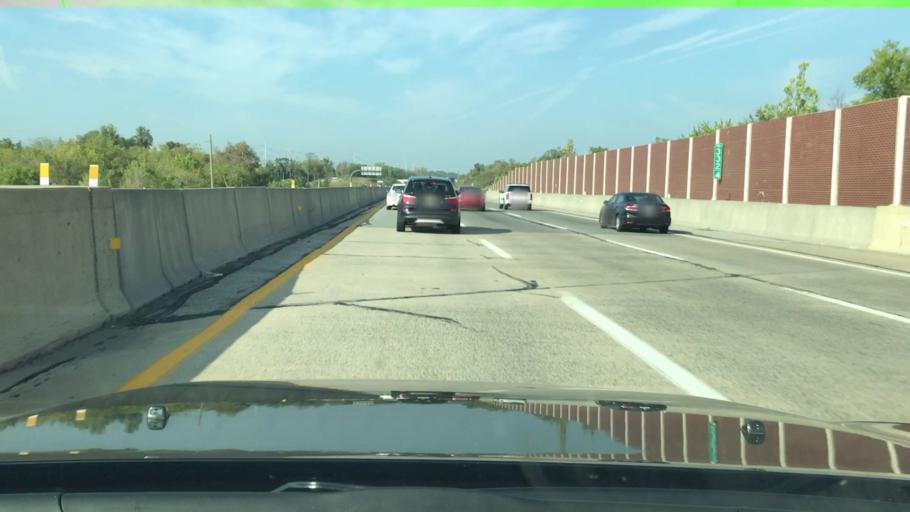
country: US
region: Pennsylvania
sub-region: Montgomery County
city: Conshohocken
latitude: 40.1078
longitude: -75.3034
